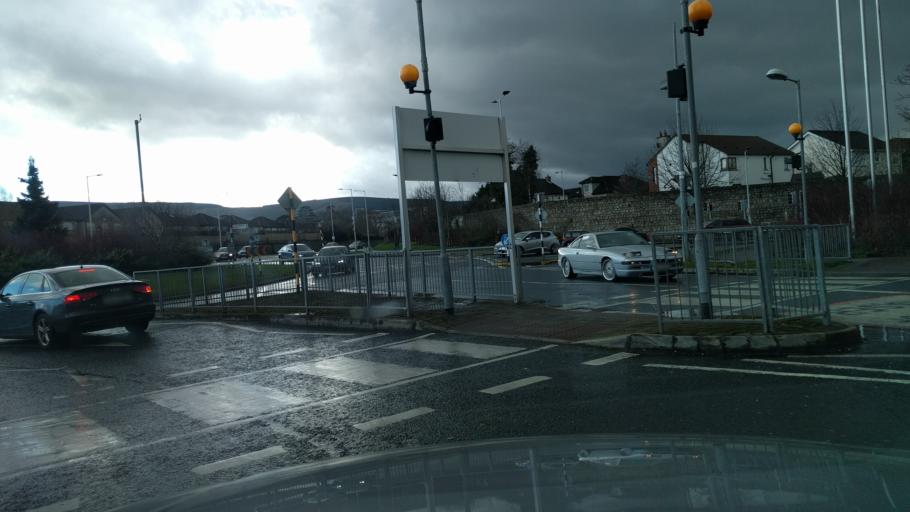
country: IE
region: Leinster
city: Balally
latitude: 53.2854
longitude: -6.2401
